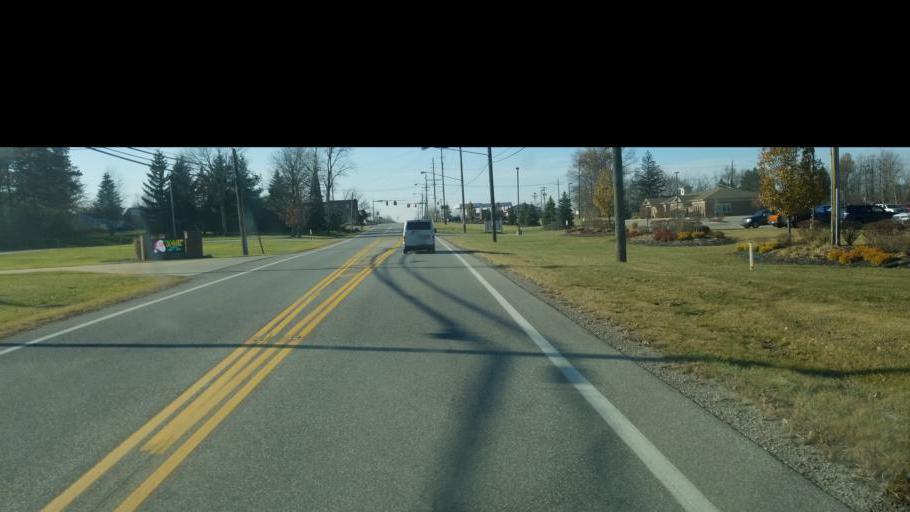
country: US
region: Ohio
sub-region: Geauga County
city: Burton
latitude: 41.4633
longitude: -81.2416
